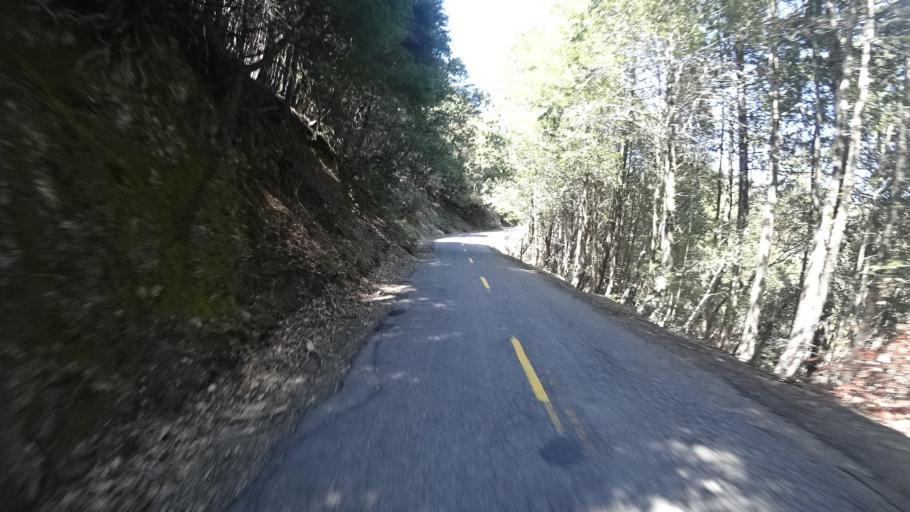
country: US
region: California
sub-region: Humboldt County
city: Rio Dell
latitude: 40.2697
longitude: -124.0778
